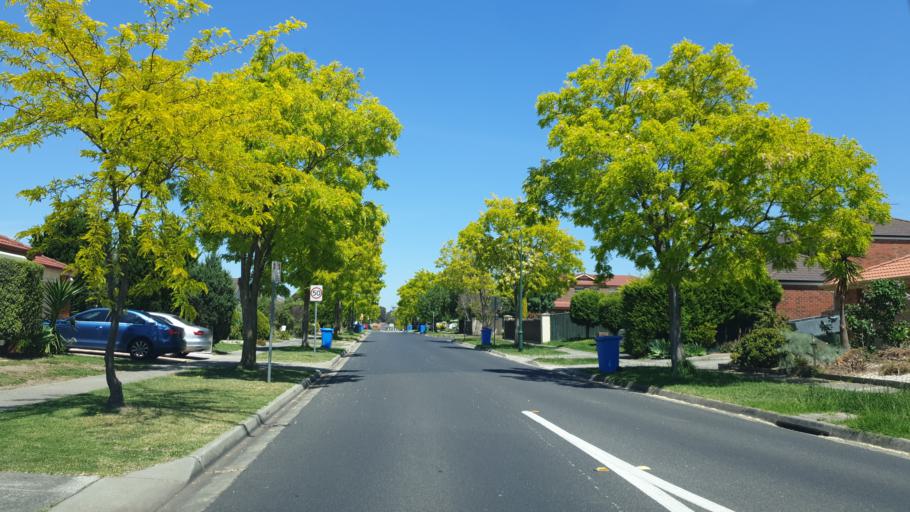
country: AU
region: Victoria
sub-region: Casey
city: Narre Warren South
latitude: -38.0628
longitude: 145.2857
